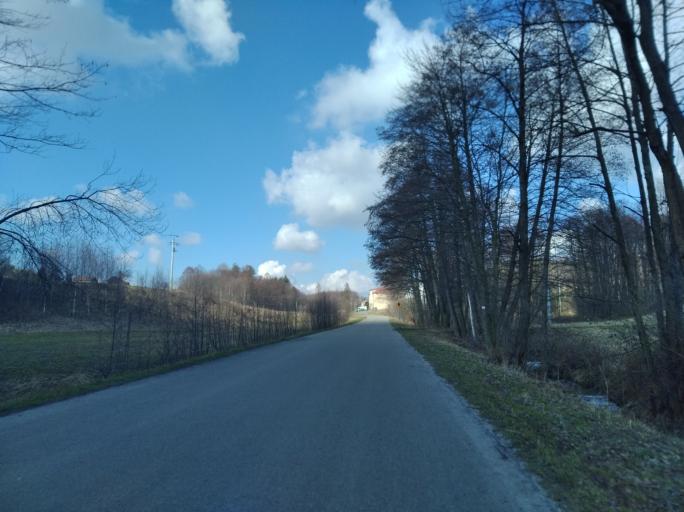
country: PL
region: Subcarpathian Voivodeship
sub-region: Powiat strzyzowski
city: Frysztak
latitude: 49.8721
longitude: 21.5282
